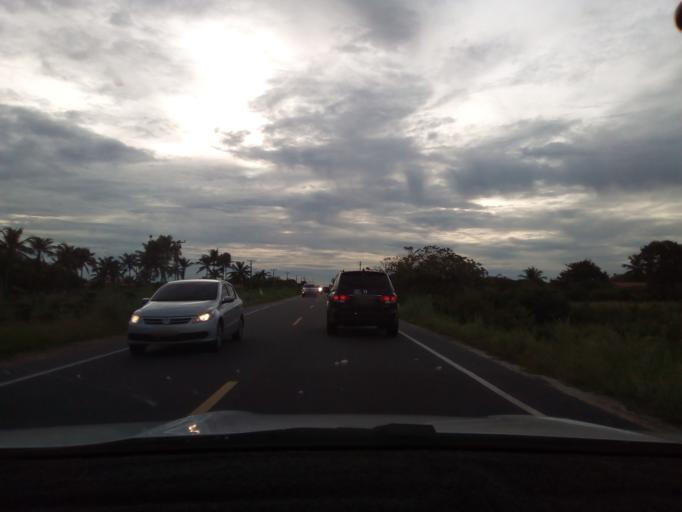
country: BR
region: Ceara
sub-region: Aracati
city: Aracati
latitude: -4.3791
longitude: -37.9122
